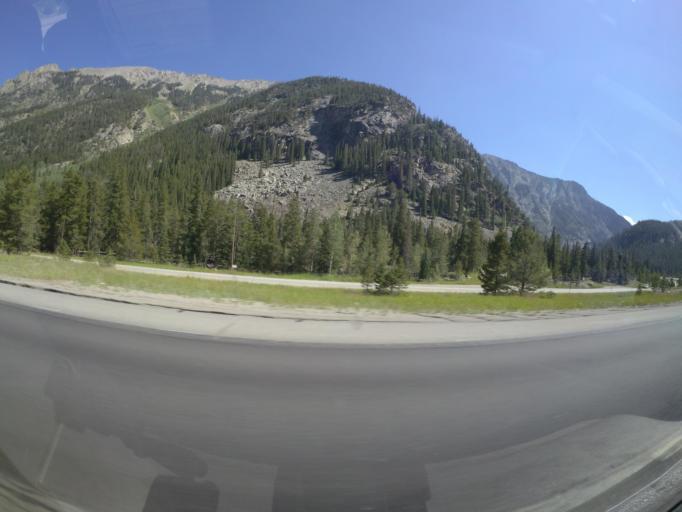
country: US
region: Colorado
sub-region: Summit County
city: Frisco
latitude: 39.5379
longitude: -106.1439
